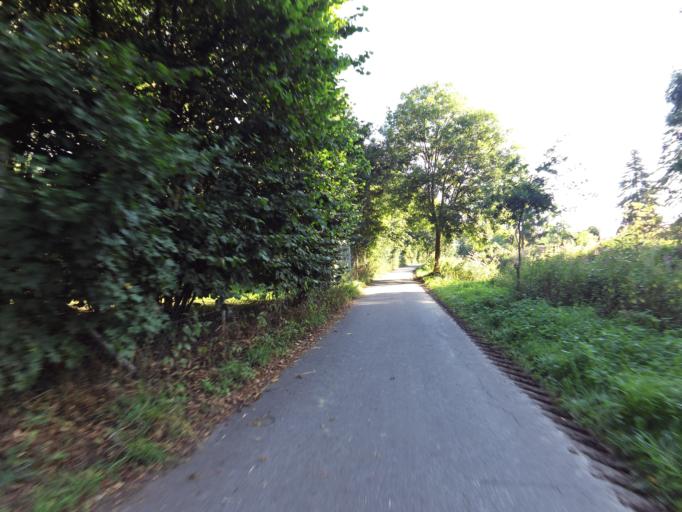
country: DE
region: North Rhine-Westphalia
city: Huckelhoven
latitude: 51.0126
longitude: 6.1768
